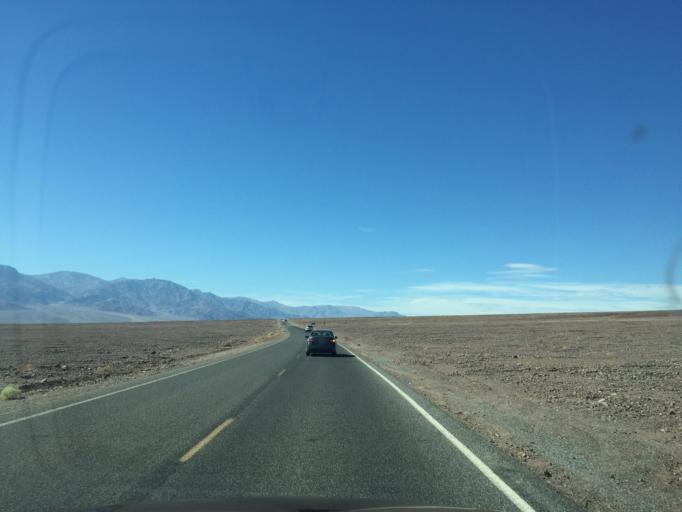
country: US
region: Nevada
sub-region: Nye County
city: Beatty
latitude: 36.2722
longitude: -116.7896
